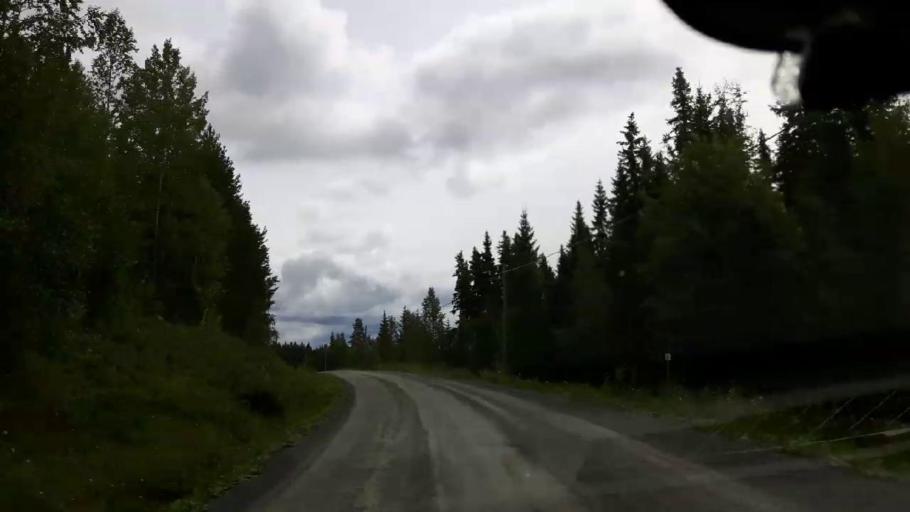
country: SE
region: Jaemtland
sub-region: Krokoms Kommun
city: Valla
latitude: 63.6805
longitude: 13.9251
